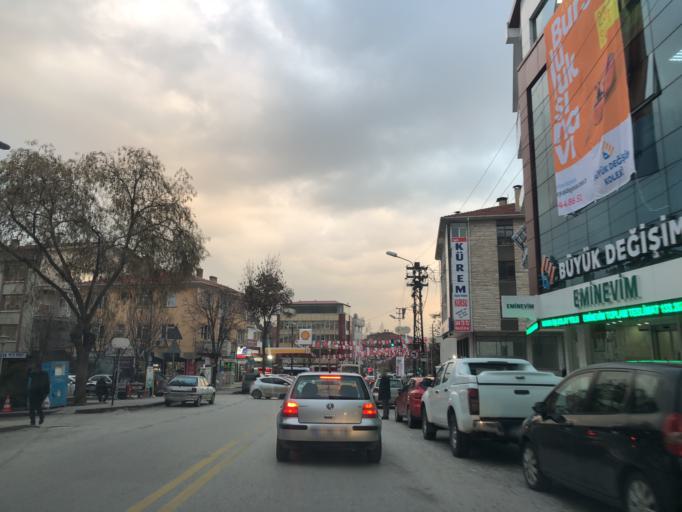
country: TR
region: Ankara
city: Ankara
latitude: 39.9672
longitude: 32.8084
